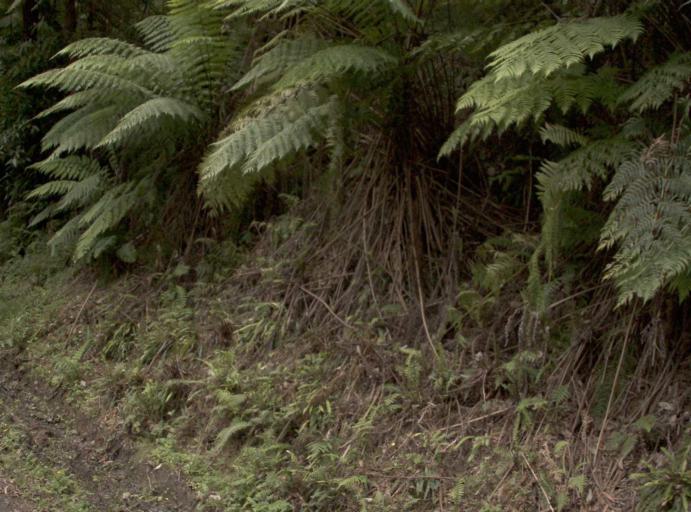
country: AU
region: Victoria
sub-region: Latrobe
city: Traralgon
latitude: -38.4625
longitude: 146.5483
